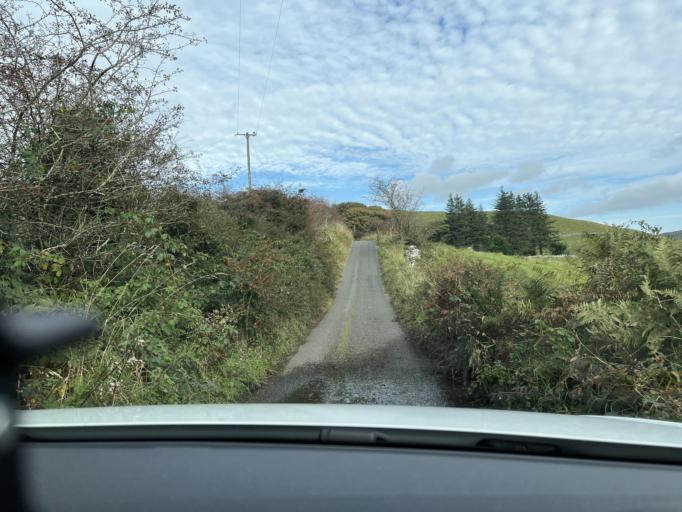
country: IE
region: Connaught
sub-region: Sligo
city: Ballymote
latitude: 54.0515
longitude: -8.4279
